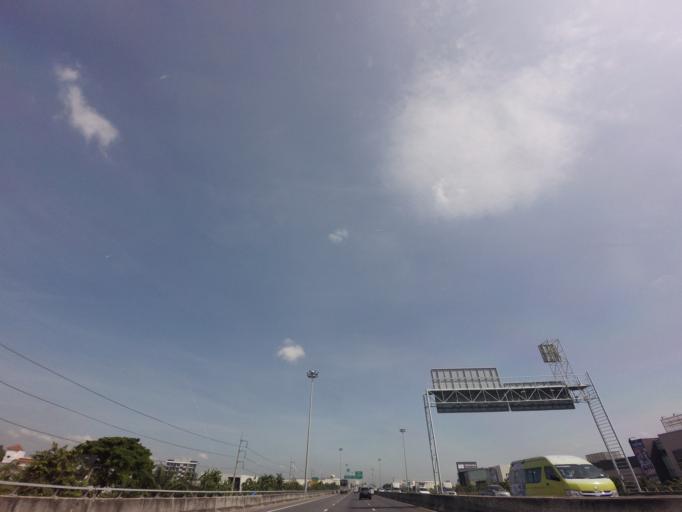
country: TH
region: Bangkok
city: Lat Phrao
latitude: 13.8049
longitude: 100.6170
